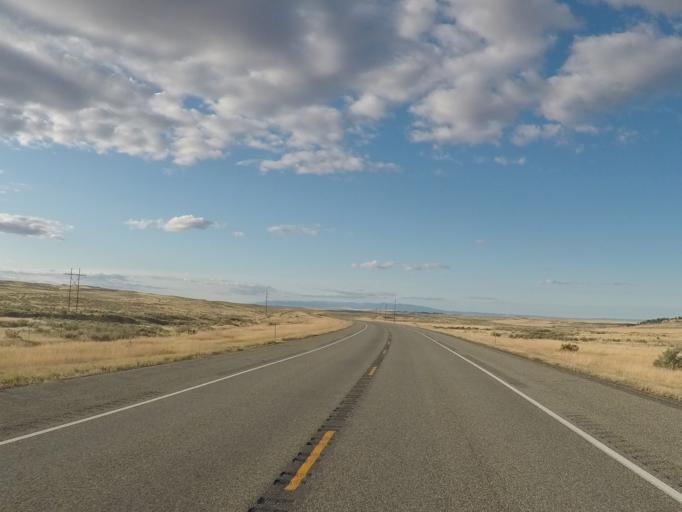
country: US
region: Montana
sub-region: Golden Valley County
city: Ryegate
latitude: 46.1656
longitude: -108.9015
